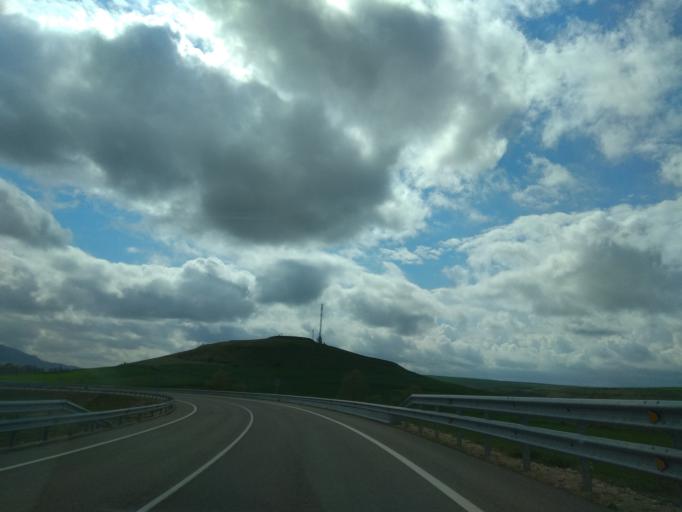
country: ES
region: Castille and Leon
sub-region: Provincia de Burgos
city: Cubo de Bureba
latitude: 42.6368
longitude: -3.1972
